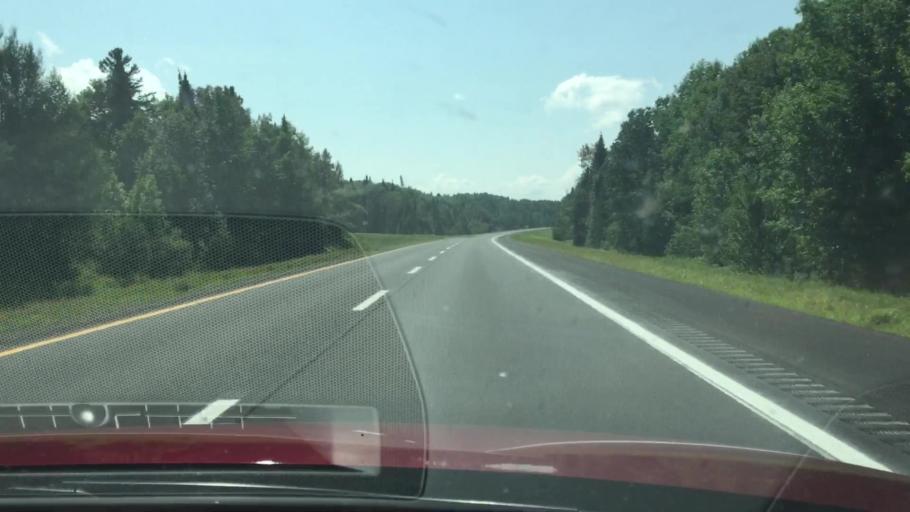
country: US
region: Maine
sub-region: Penobscot County
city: Patten
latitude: 45.9216
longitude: -68.3689
